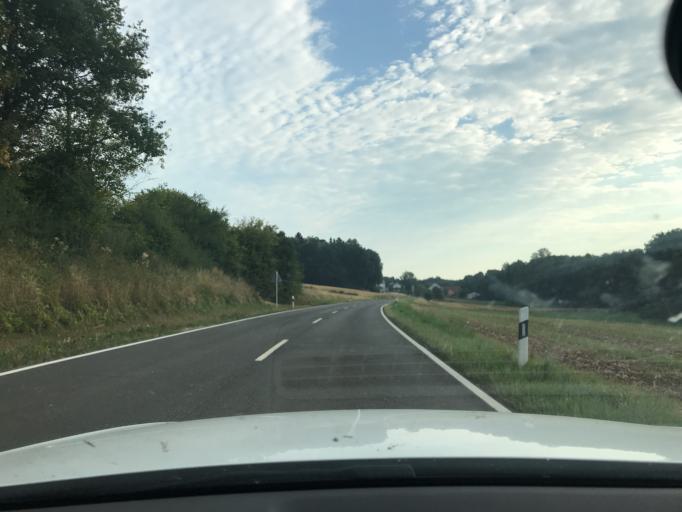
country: DE
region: Bavaria
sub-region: Upper Franconia
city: Pegnitz
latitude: 49.7486
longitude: 11.6049
